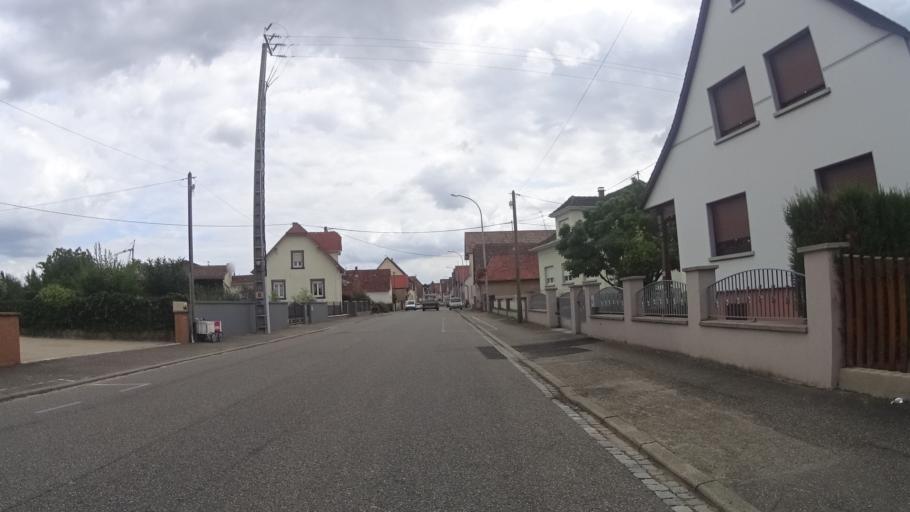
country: FR
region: Alsace
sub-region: Departement du Bas-Rhin
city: Geudertheim
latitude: 48.7232
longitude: 7.7440
